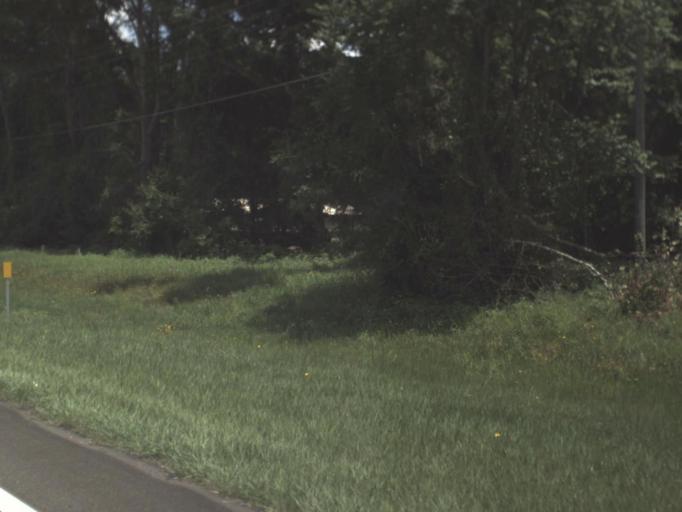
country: US
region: Florida
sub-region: Alachua County
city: High Springs
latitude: 29.8233
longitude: -82.5880
